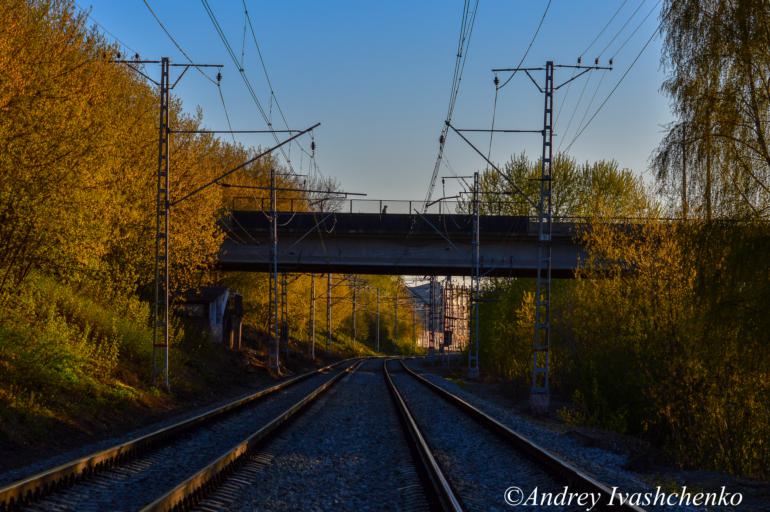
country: RU
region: Perm
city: Perm
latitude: 58.0158
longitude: 56.2249
